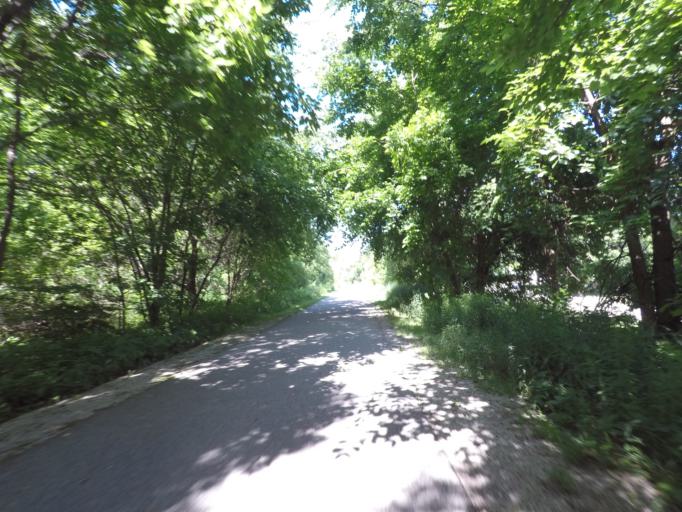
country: US
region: Wisconsin
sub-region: Milwaukee County
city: West Allis
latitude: 43.0244
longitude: -87.9921
